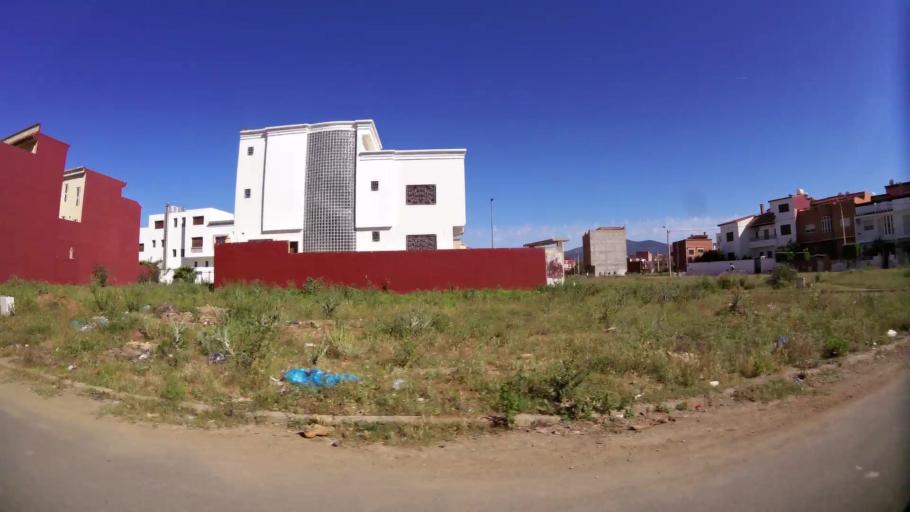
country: MA
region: Oriental
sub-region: Berkane-Taourirt
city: Berkane
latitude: 34.9420
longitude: -2.3383
